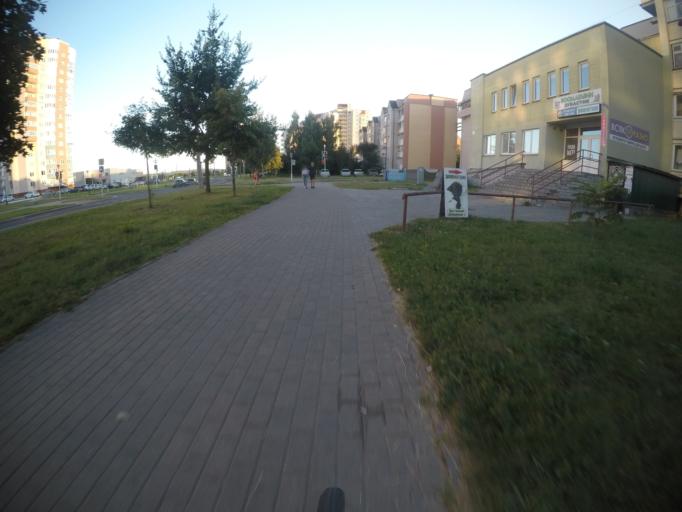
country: BY
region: Grodnenskaya
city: Hrodna
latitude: 53.7129
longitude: 23.8581
